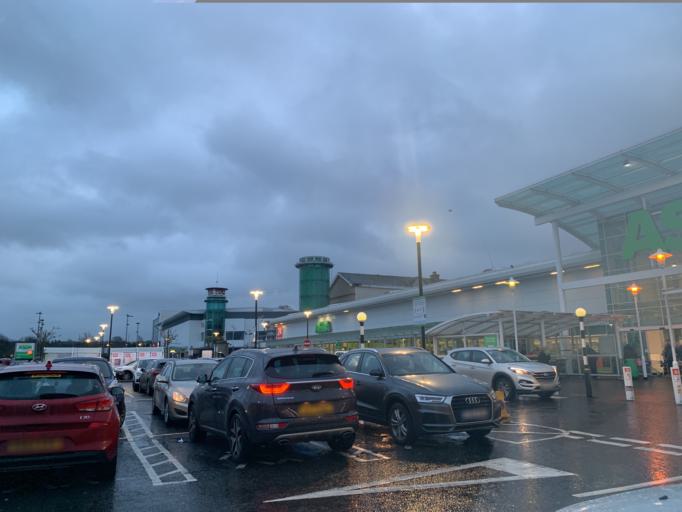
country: GB
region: Scotland
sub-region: South Lanarkshire
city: Hamilton
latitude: 55.7787
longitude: -4.0320
